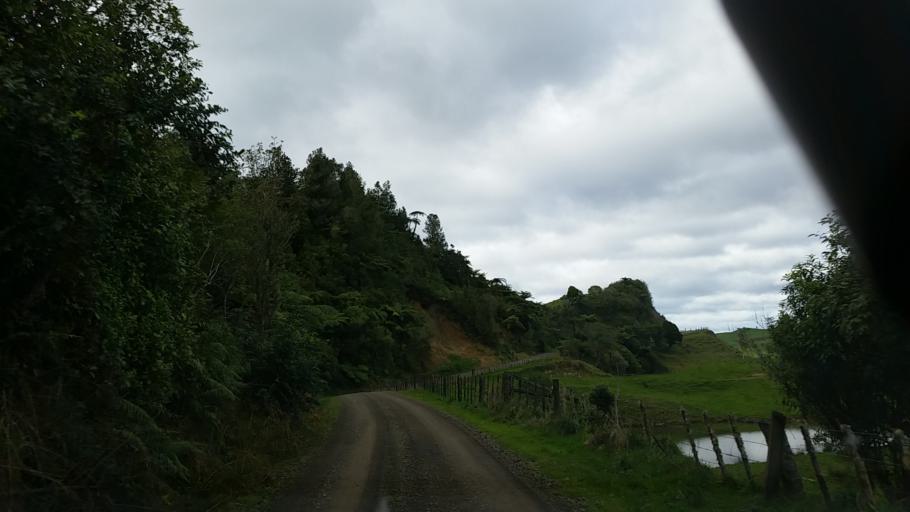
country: NZ
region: Taranaki
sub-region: New Plymouth District
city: Waitara
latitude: -39.0221
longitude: 174.5557
